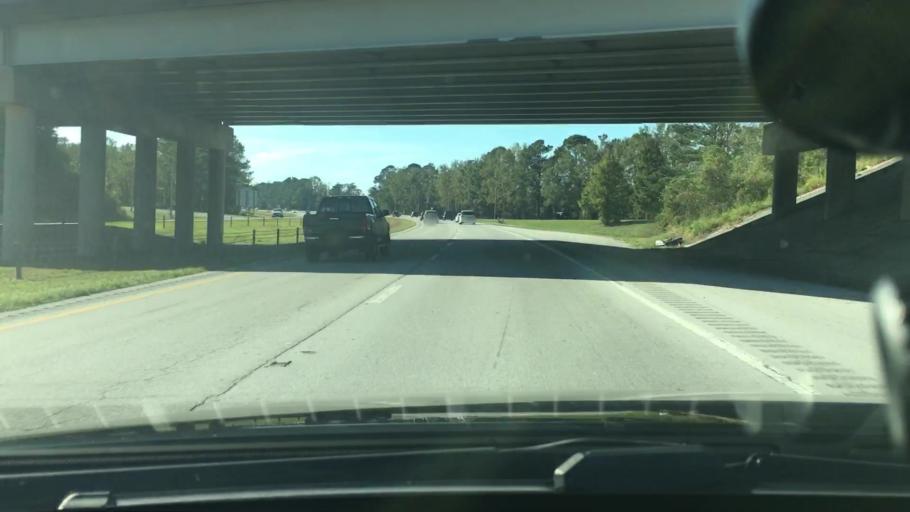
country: US
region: North Carolina
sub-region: Craven County
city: New Bern
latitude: 35.1011
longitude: -77.0583
